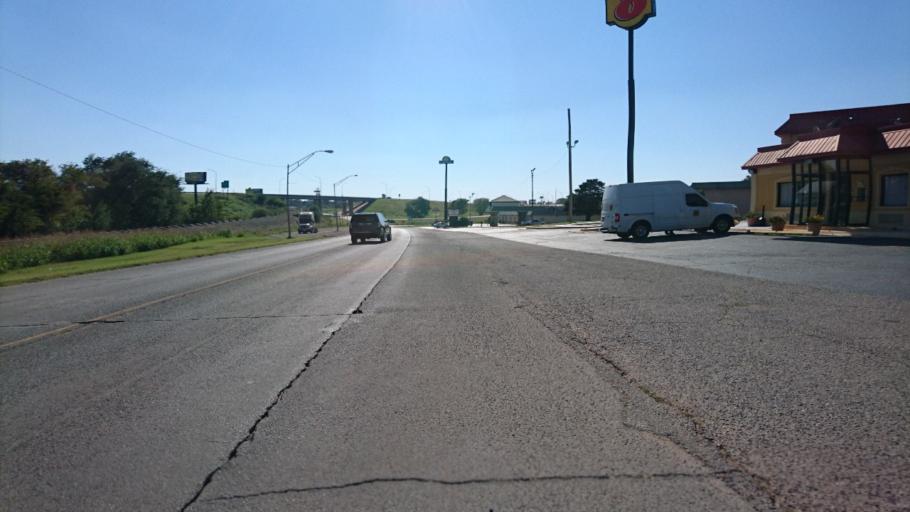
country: US
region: Oklahoma
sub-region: Custer County
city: Clinton
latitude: 35.5018
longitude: -98.9740
